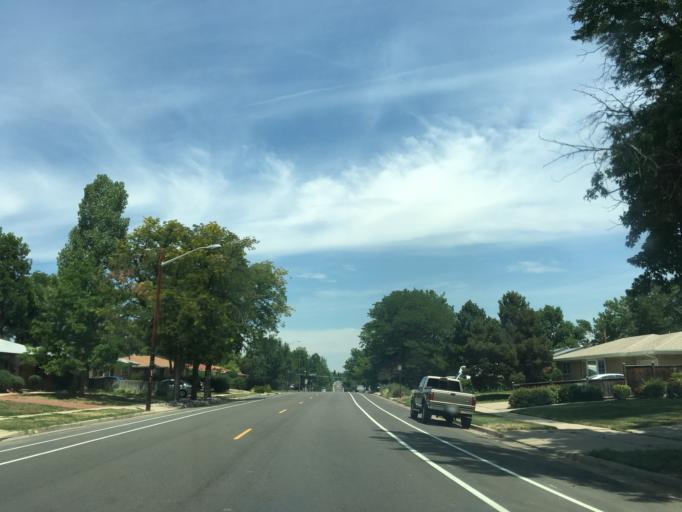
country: US
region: Colorado
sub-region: Arapahoe County
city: Sheridan
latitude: 39.6803
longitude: -105.0443
